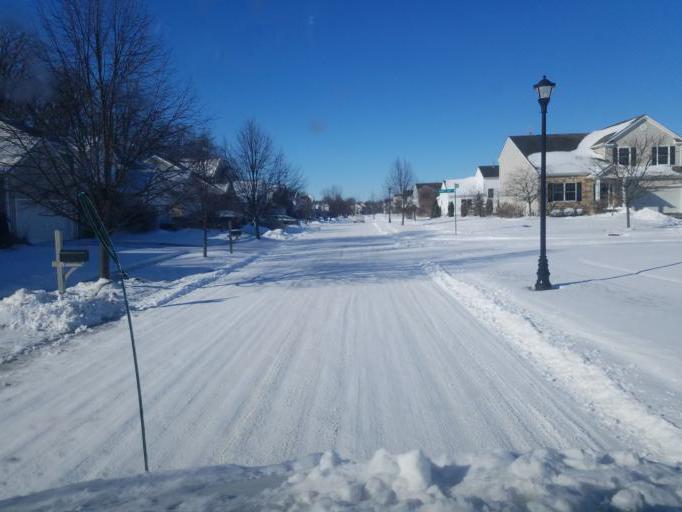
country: US
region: Ohio
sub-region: Franklin County
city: Worthington
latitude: 40.1438
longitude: -83.0095
